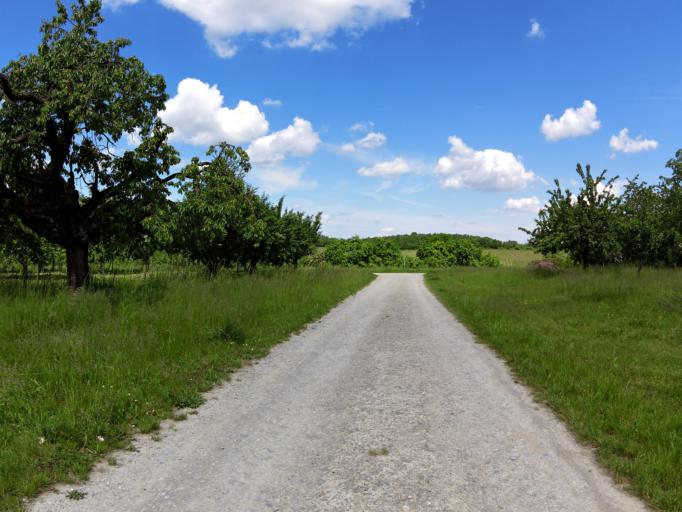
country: DE
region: Bavaria
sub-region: Regierungsbezirk Unterfranken
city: Winterhausen
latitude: 49.7277
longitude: 10.0223
